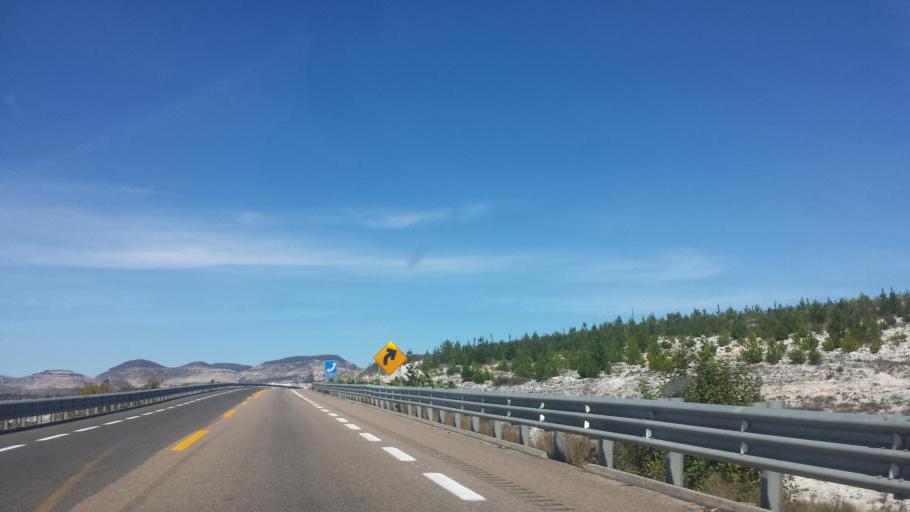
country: MX
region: Oaxaca
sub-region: Villa Tejupam de la Union
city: Villa Tejupam de la Union
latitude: 17.8495
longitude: -97.3780
